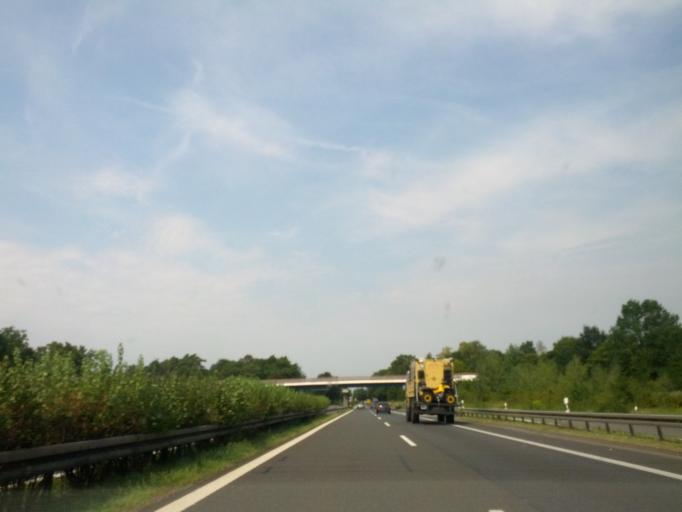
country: DE
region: Brandenburg
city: Werder
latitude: 52.4330
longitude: 12.9301
